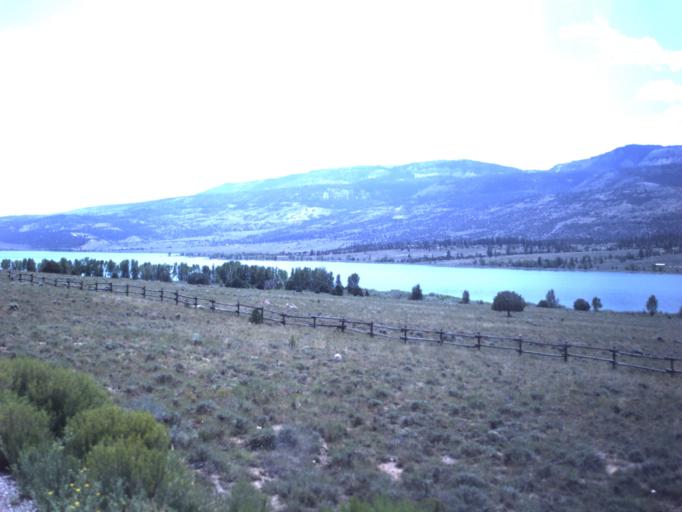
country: US
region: Utah
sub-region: Emery County
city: Orangeville
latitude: 39.3148
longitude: -111.2759
